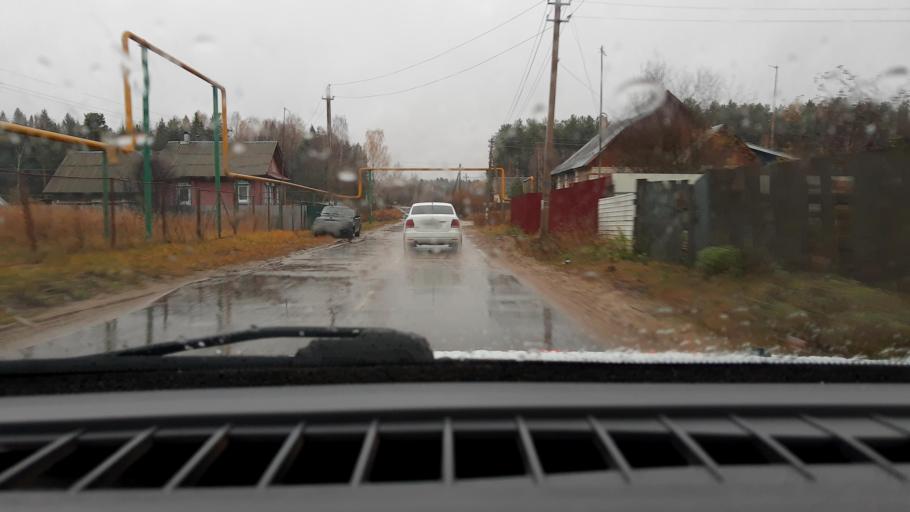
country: RU
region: Nizjnij Novgorod
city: Linda
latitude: 56.6809
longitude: 44.1959
